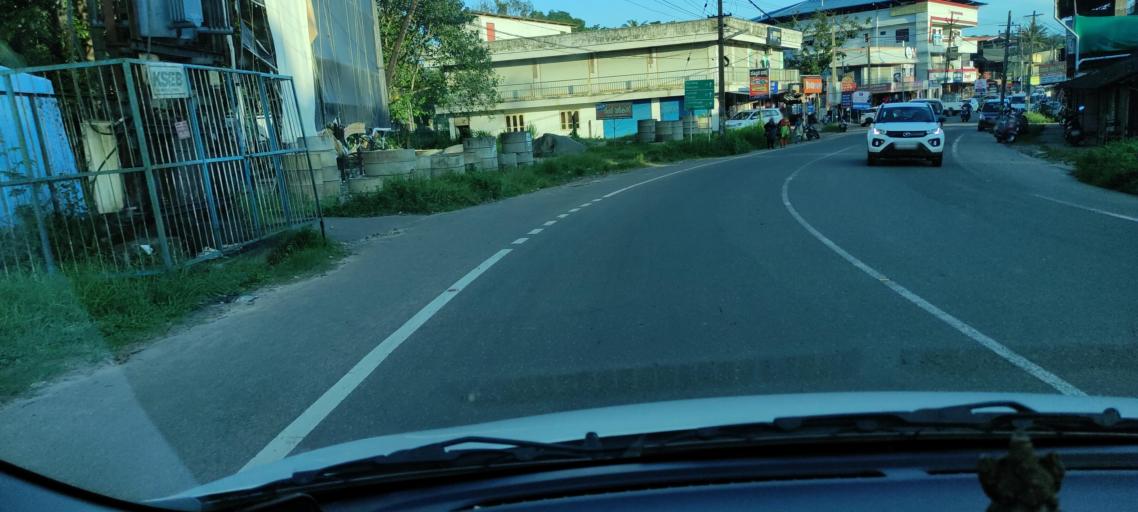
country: IN
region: Kerala
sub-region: Pattanamtitta
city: Adur
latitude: 9.1469
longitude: 76.7640
